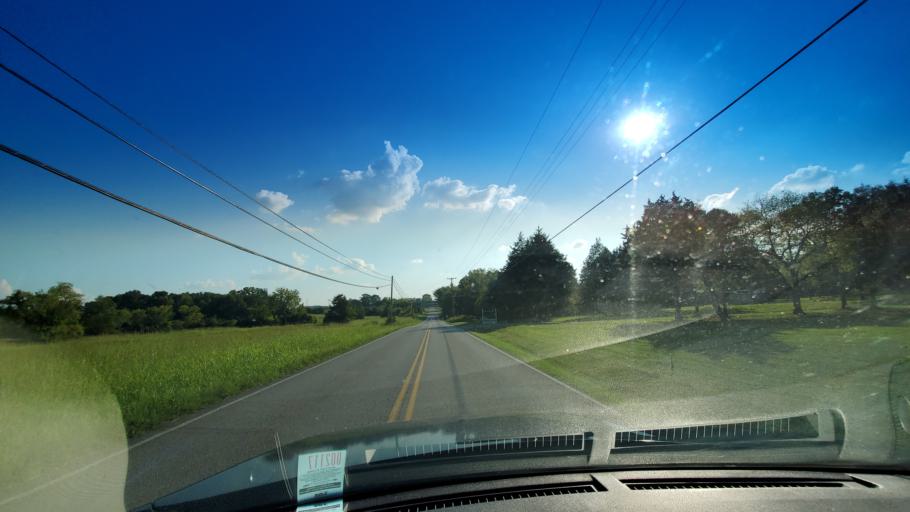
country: US
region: Tennessee
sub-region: Wilson County
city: Lebanon
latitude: 36.1768
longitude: -86.3496
